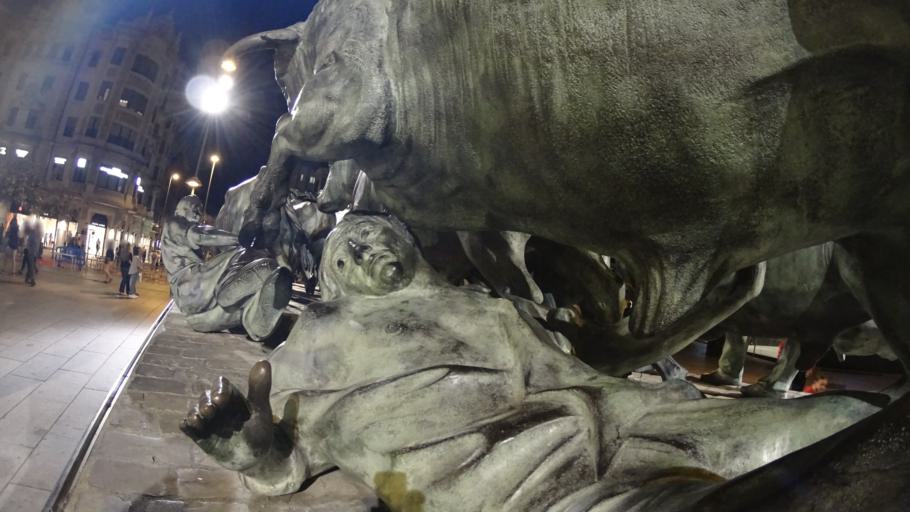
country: ES
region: Navarre
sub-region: Provincia de Navarra
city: Segundo Ensanche
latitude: 42.8147
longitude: -1.6413
